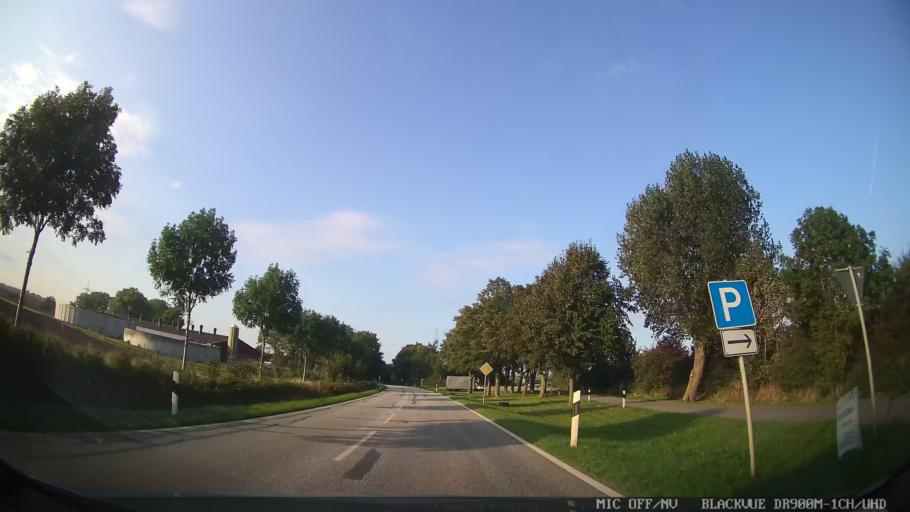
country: DE
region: Schleswig-Holstein
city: Heiligenhafen
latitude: 54.3565
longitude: 11.0110
